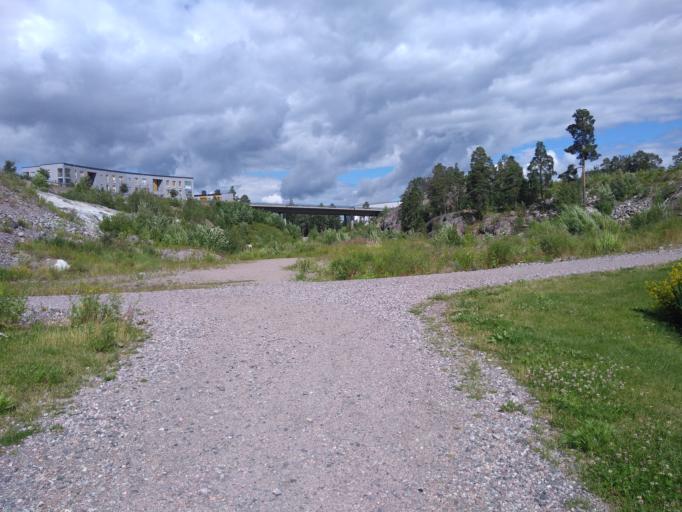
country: FI
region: Uusimaa
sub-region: Helsinki
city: Helsinki
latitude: 60.2274
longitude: 24.9909
